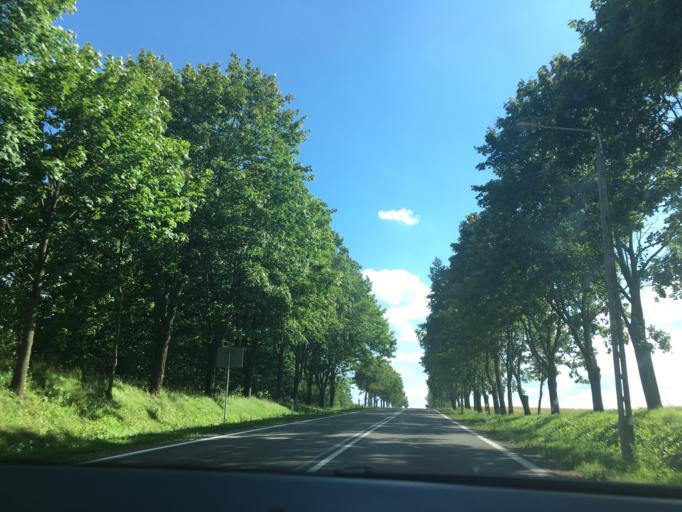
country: PL
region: Podlasie
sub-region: Powiat sokolski
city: Janow
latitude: 53.3929
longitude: 23.1139
